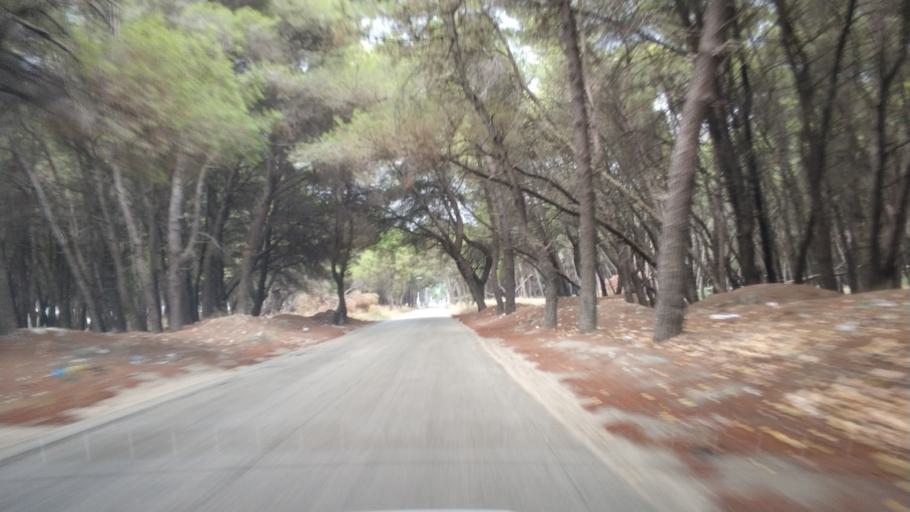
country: AL
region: Vlore
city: Vlore
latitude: 40.4688
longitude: 19.4603
